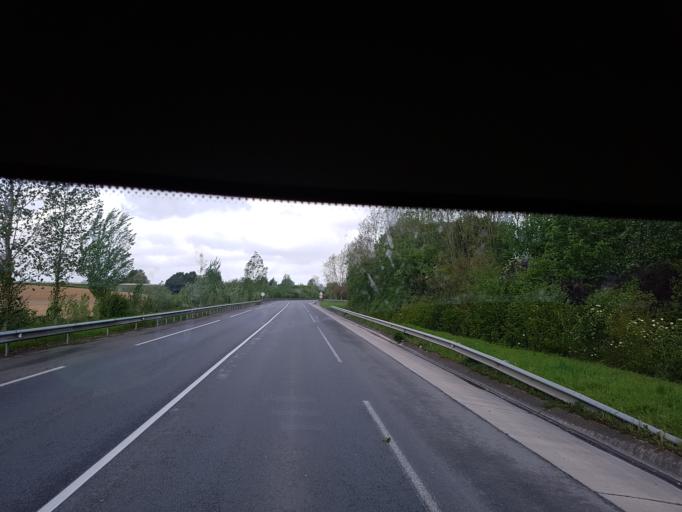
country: FR
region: Nord-Pas-de-Calais
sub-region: Departement du Nord
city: Proville
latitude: 50.1795
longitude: 3.1922
